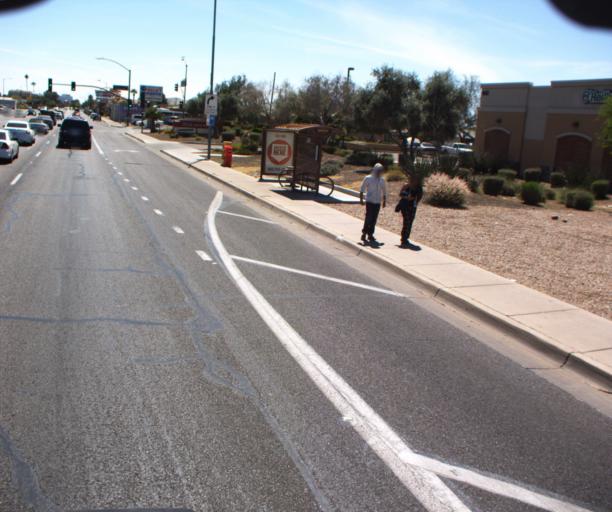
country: US
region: Arizona
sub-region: Maricopa County
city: Chandler
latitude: 33.3143
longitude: -111.8416
